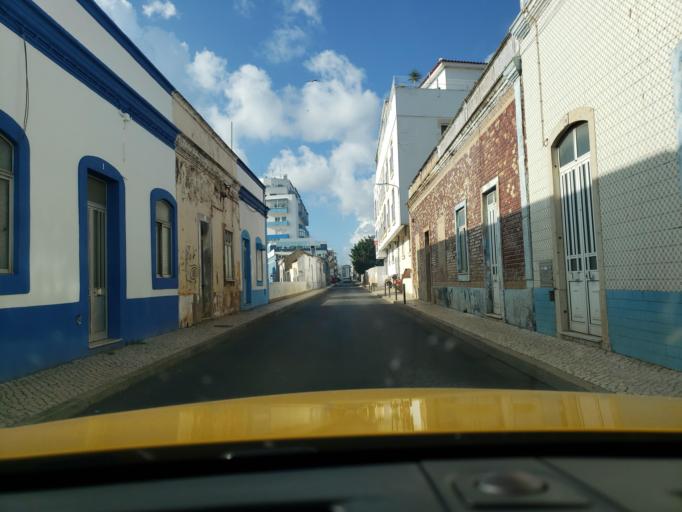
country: PT
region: Faro
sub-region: Portimao
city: Portimao
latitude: 37.1403
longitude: -8.5326
